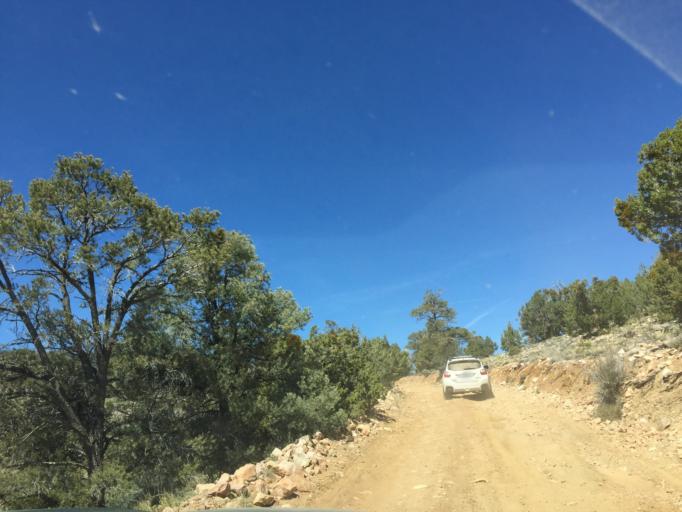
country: US
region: California
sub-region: San Bernardino County
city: Big Bear City
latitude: 34.2487
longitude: -116.7142
